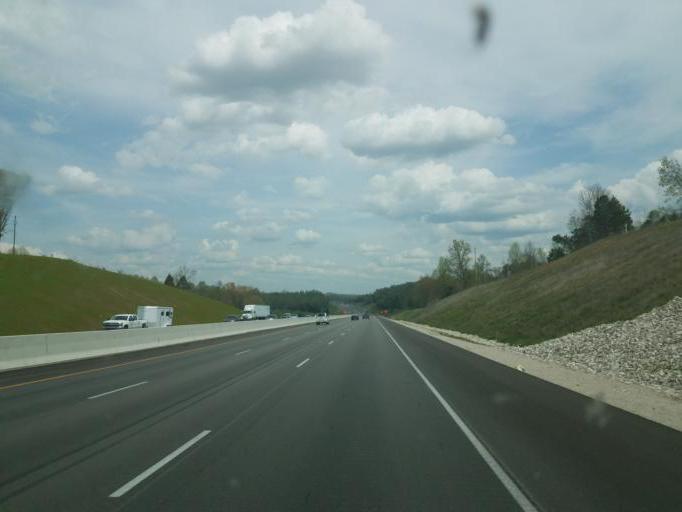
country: US
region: Kentucky
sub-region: Hart County
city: Munfordville
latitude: 37.3573
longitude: -85.8972
